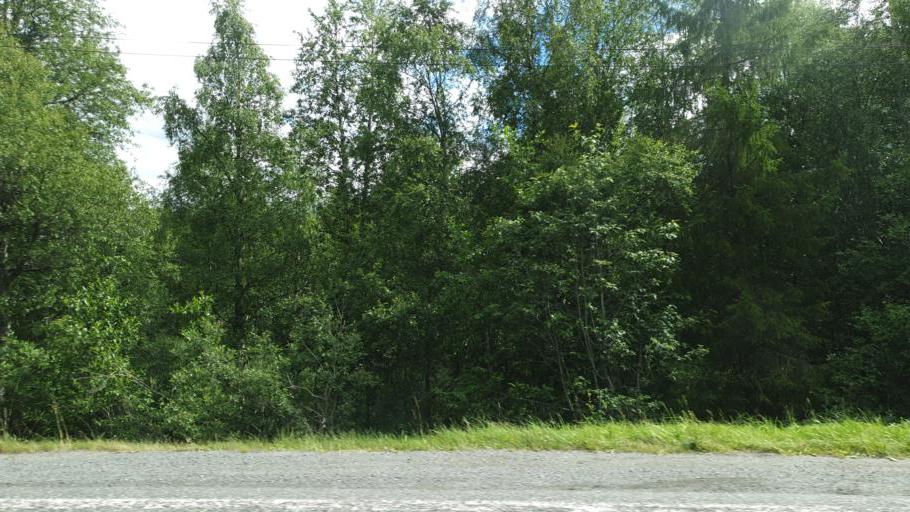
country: NO
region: Sor-Trondelag
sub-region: Rennebu
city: Berkak
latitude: 62.8529
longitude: 10.0206
